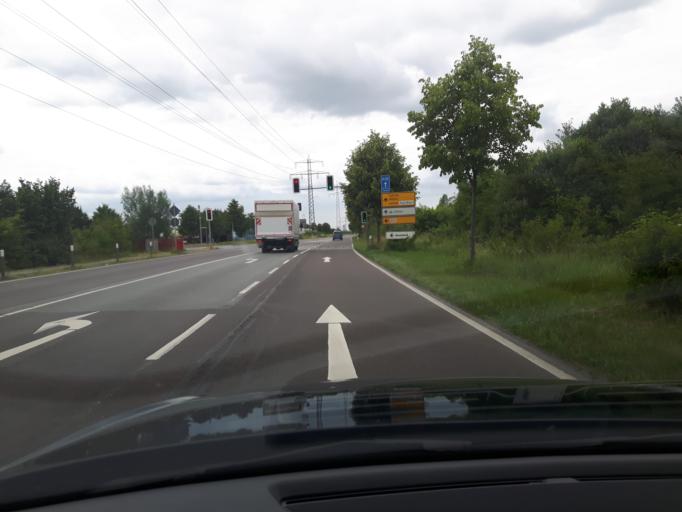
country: DE
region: Lower Saxony
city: Lehrte
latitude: 52.3863
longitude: 9.9542
